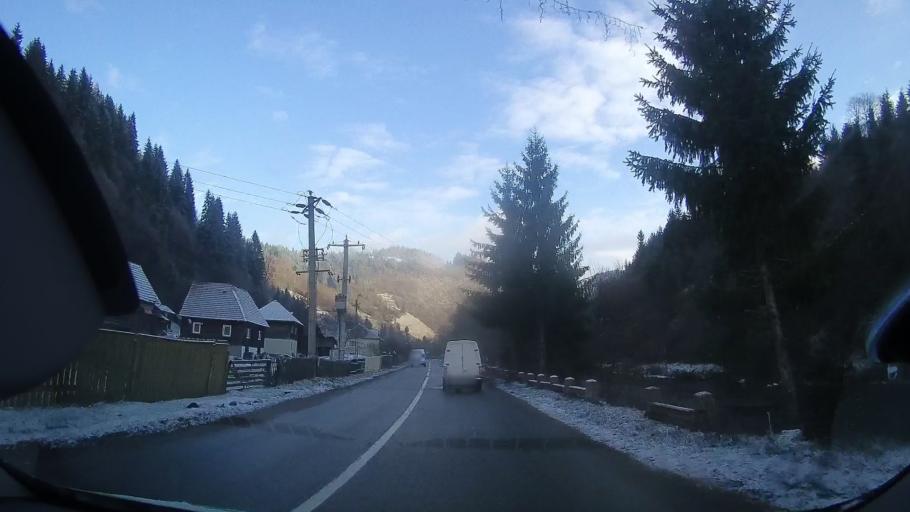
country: RO
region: Alba
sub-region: Comuna Scarisoara
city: Scarisoara
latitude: 46.4580
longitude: 22.8785
